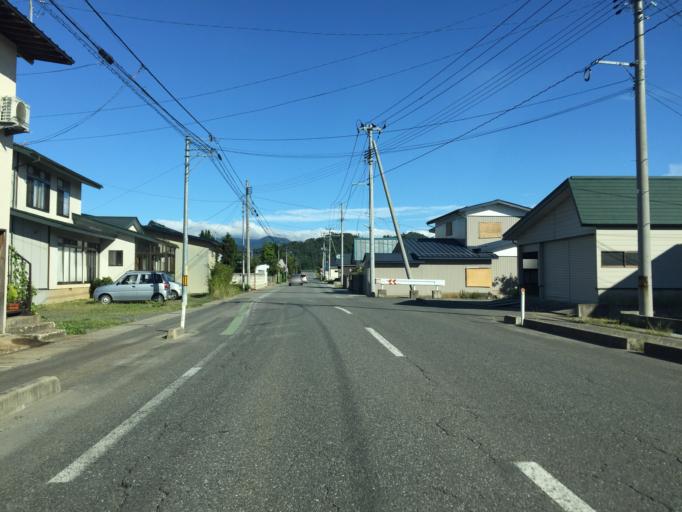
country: JP
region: Yamagata
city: Yonezawa
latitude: 37.9553
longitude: 140.1282
